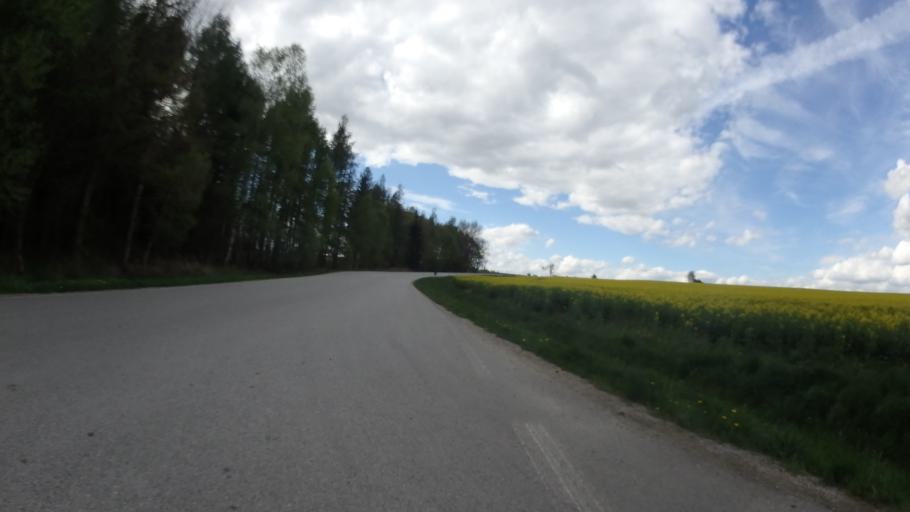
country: CZ
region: Vysocina
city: Merin
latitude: 49.3735
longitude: 15.8925
